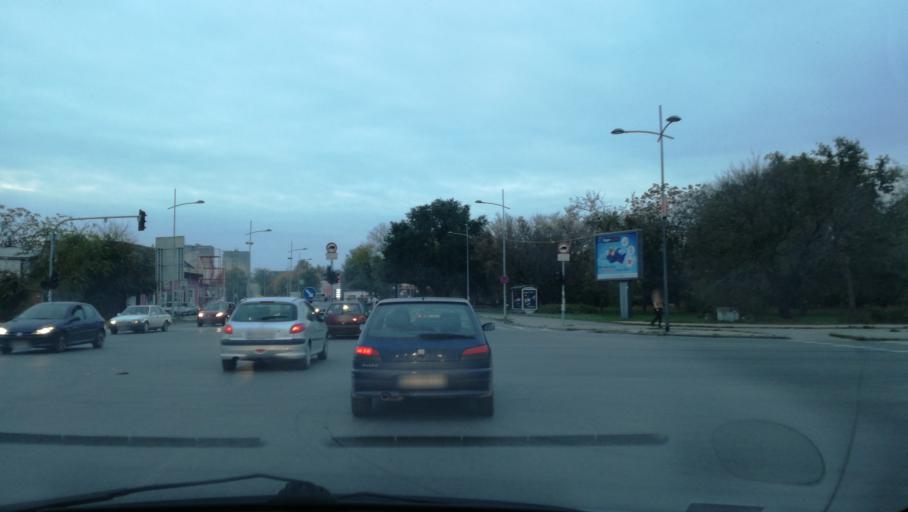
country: RS
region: Autonomna Pokrajina Vojvodina
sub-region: Juznobacki Okrug
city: Novi Sad
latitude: 45.2695
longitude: 19.8316
